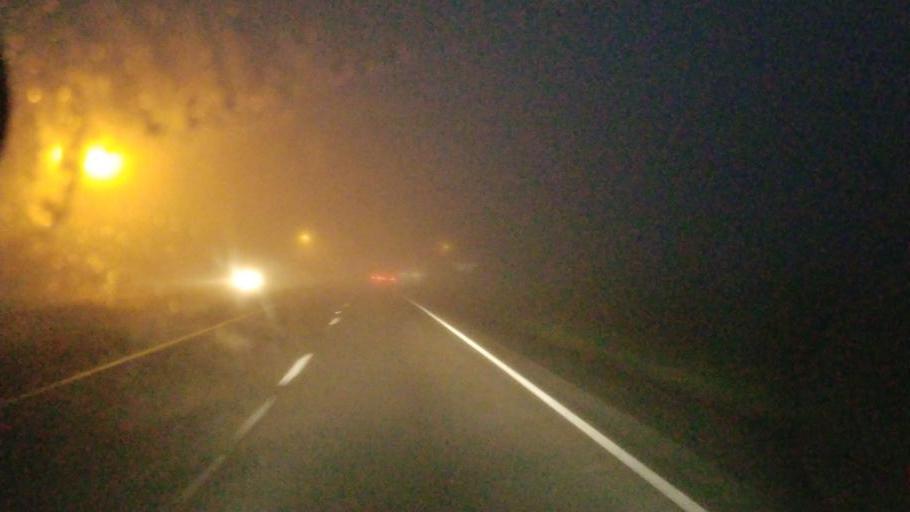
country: US
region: Ohio
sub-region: Ross County
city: Chillicothe
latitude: 39.3939
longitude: -82.9711
